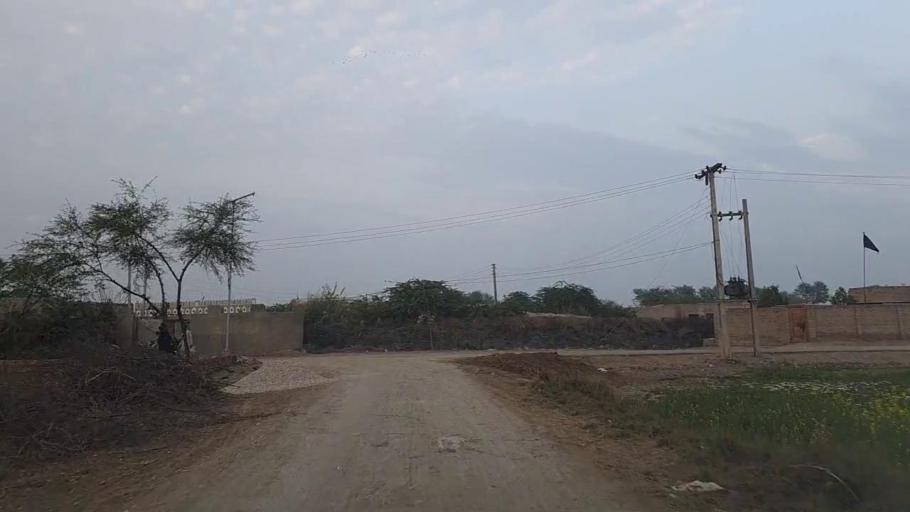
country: PK
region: Sindh
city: Jam Sahib
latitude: 26.2984
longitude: 68.5935
